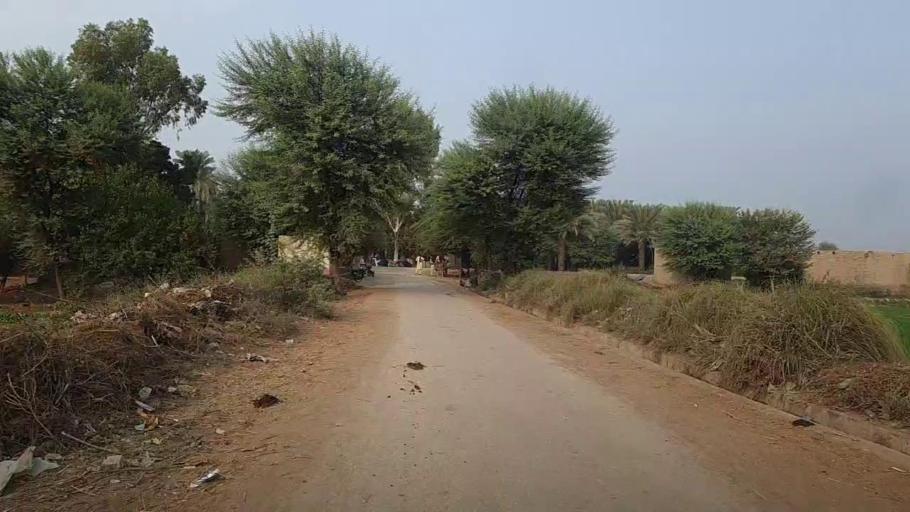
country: PK
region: Sindh
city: Setharja Old
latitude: 27.1004
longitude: 68.5054
